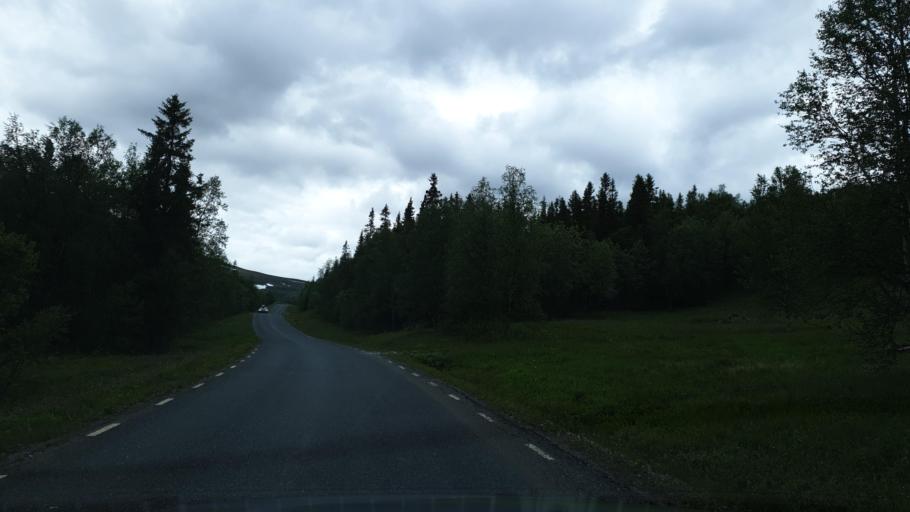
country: SE
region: Vaesterbotten
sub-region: Vilhelmina Kommun
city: Sjoberg
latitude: 65.2797
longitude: 15.3101
